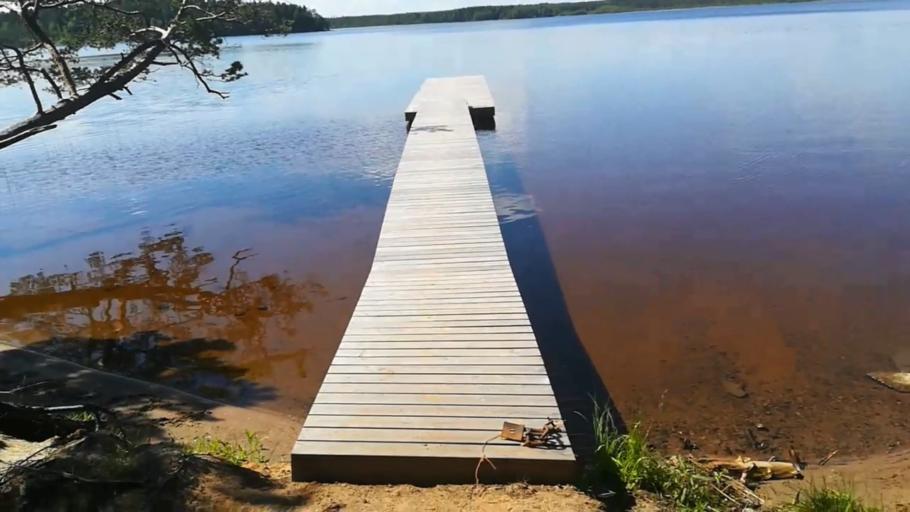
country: FI
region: Southern Savonia
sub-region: Pieksaemaeki
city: Juva
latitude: 61.8824
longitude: 27.8860
